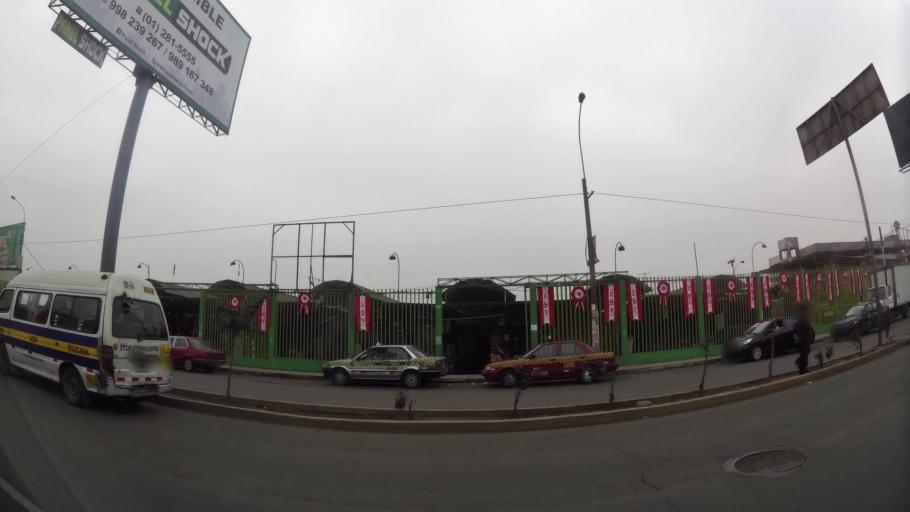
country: PE
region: Lima
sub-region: Lima
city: Vitarte
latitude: -12.0433
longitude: -76.9367
